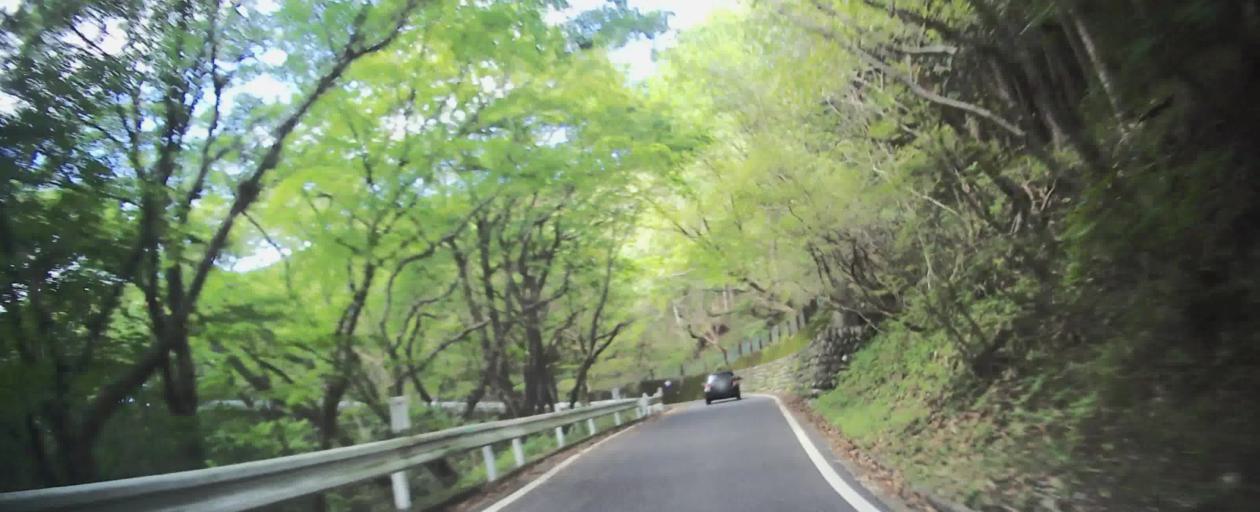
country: JP
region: Gunma
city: Shibukawa
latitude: 36.4609
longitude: 138.8932
